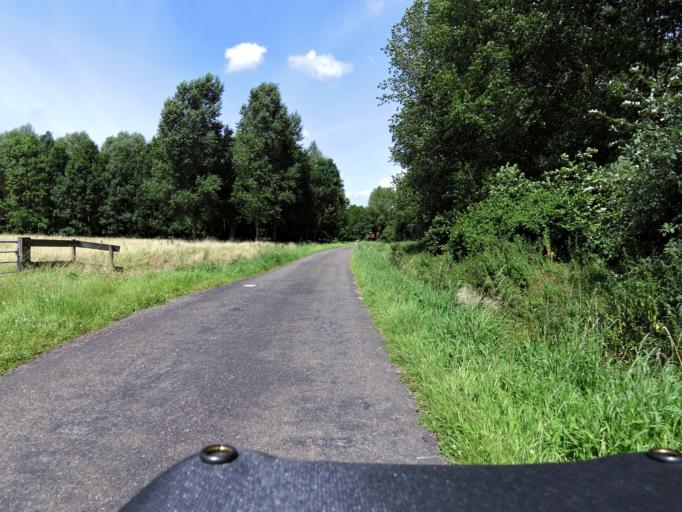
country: NL
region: South Holland
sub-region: Gemeente Albrandswaard
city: Rhoon
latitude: 51.8680
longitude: 4.4034
